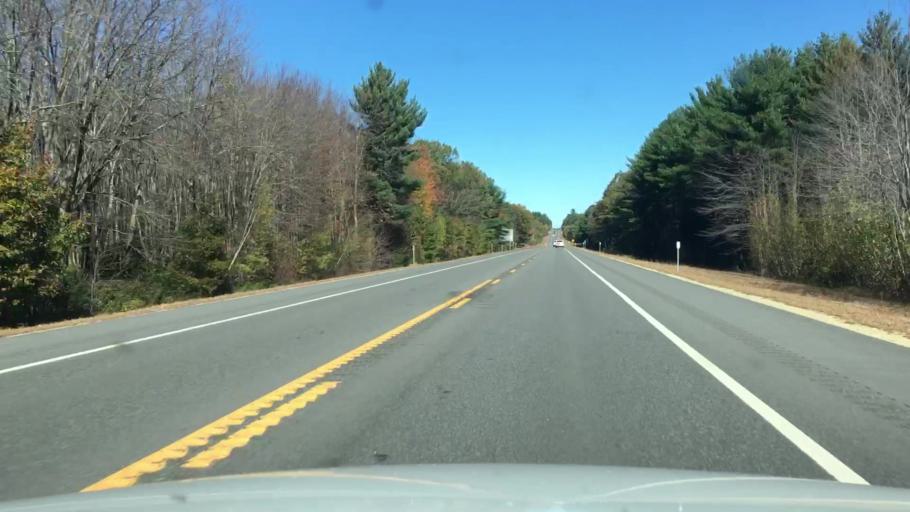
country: US
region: New Hampshire
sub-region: Strafford County
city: Rochester
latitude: 43.3440
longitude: -70.9847
